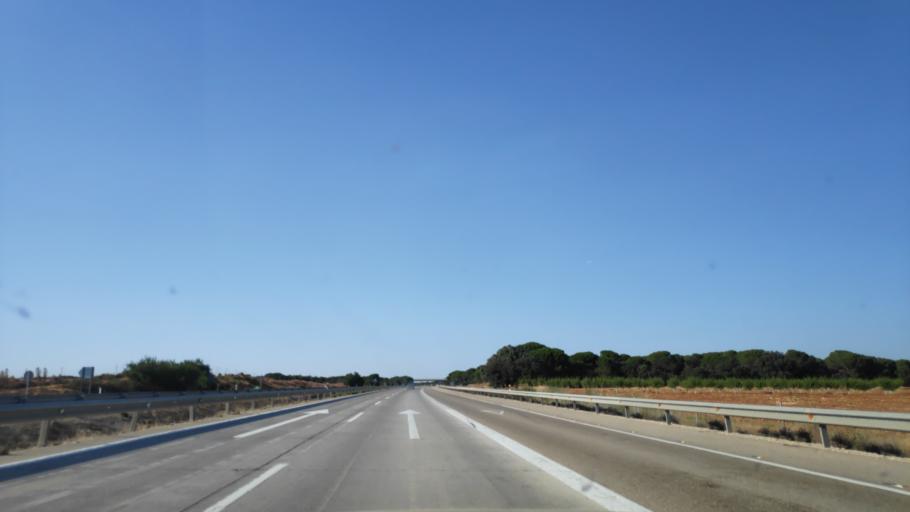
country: ES
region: Castille-La Mancha
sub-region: Provincia de Cuenca
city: Pozoamargo
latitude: 39.3245
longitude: -2.2026
